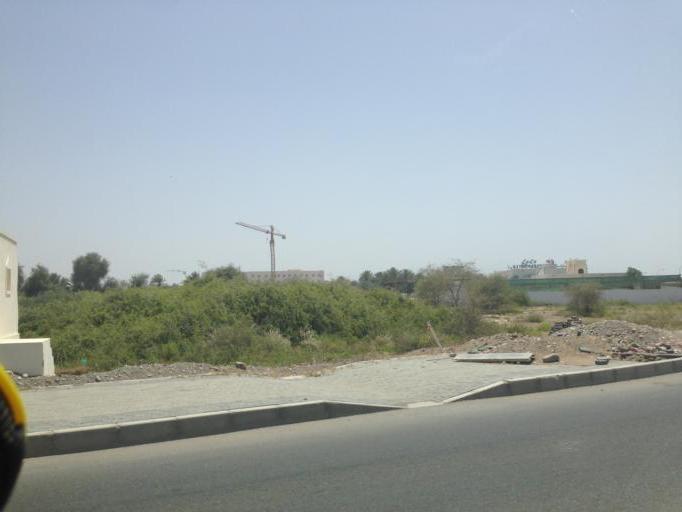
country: OM
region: Muhafazat Masqat
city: As Sib al Jadidah
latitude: 23.6826
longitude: 58.1418
